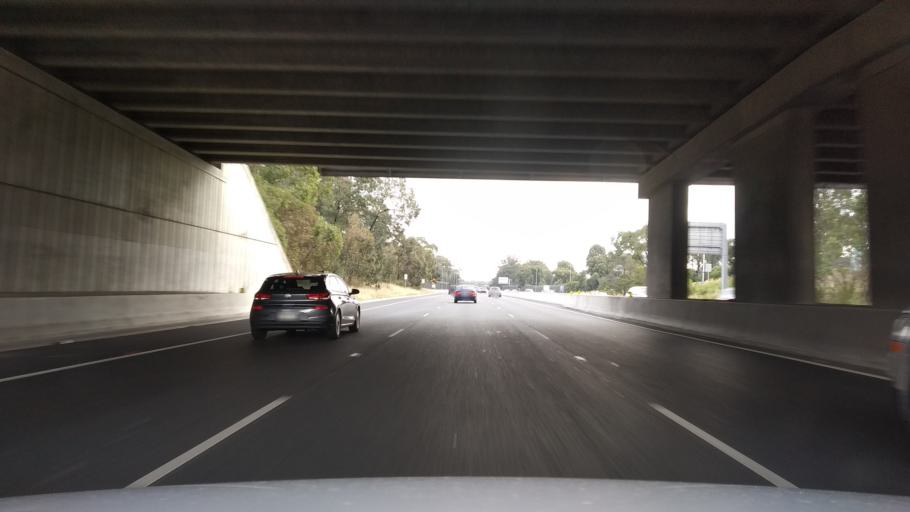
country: AU
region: New South Wales
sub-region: Hurstville
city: Peakhurst
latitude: -33.9428
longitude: 151.0541
